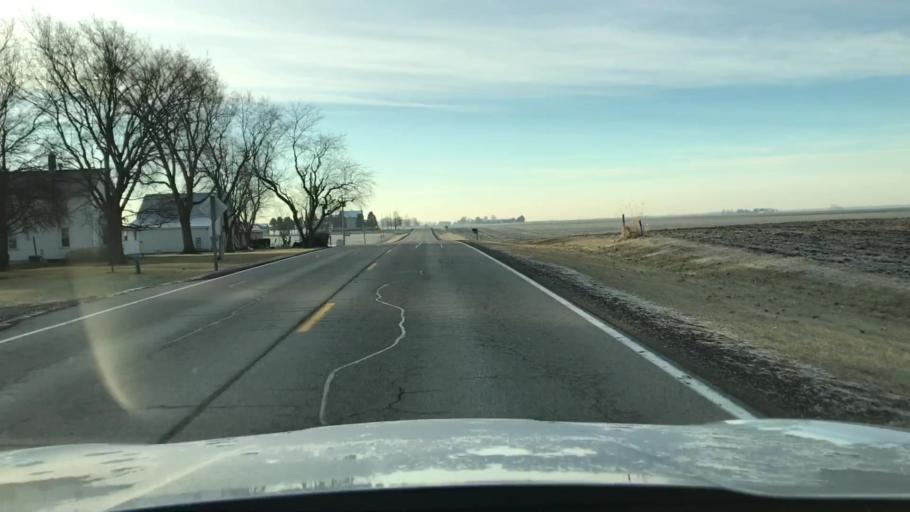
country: US
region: Illinois
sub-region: McLean County
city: Hudson
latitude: 40.6038
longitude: -88.9451
